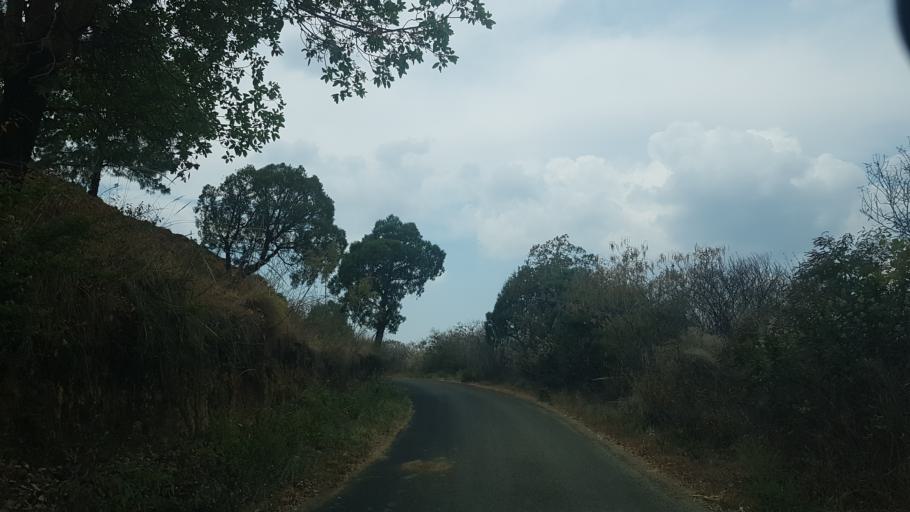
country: MX
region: Puebla
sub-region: Atzitzihuacan
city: Santiago Atzitzihuacan
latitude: 18.8379
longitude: -98.6171
